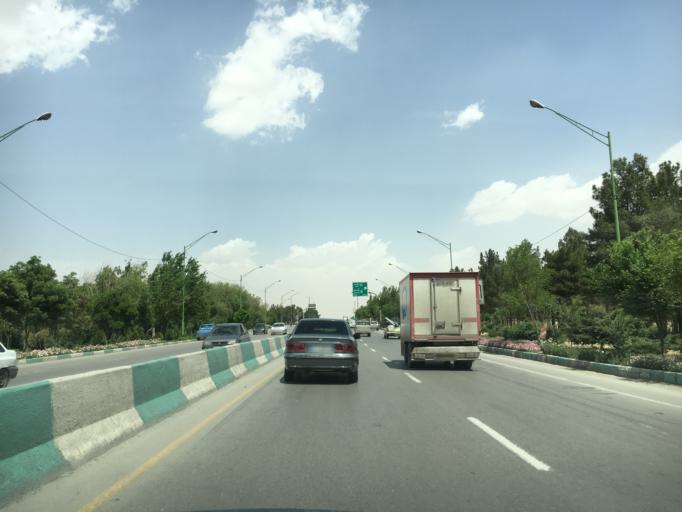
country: IR
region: Isfahan
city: Isfahan
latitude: 32.6961
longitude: 51.7340
